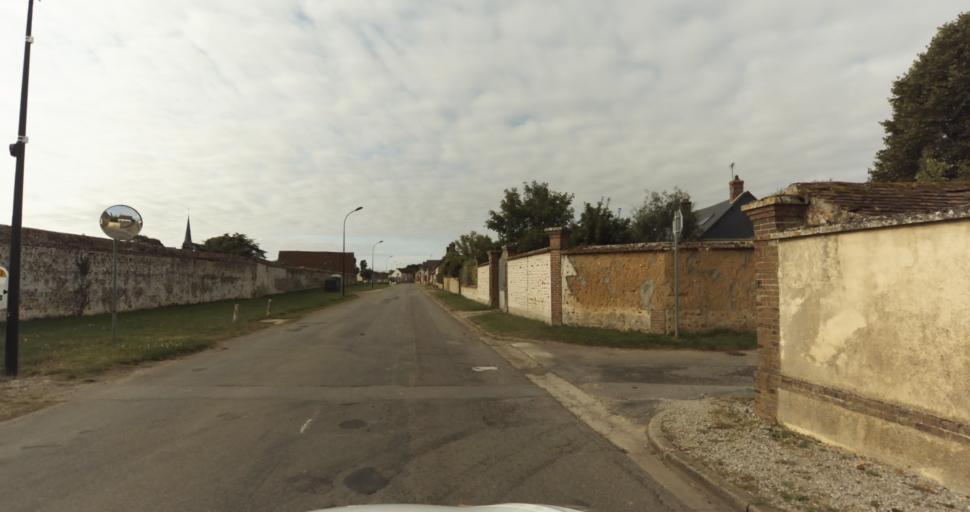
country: FR
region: Haute-Normandie
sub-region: Departement de l'Eure
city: La Madeleine-de-Nonancourt
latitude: 48.8670
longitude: 1.2471
